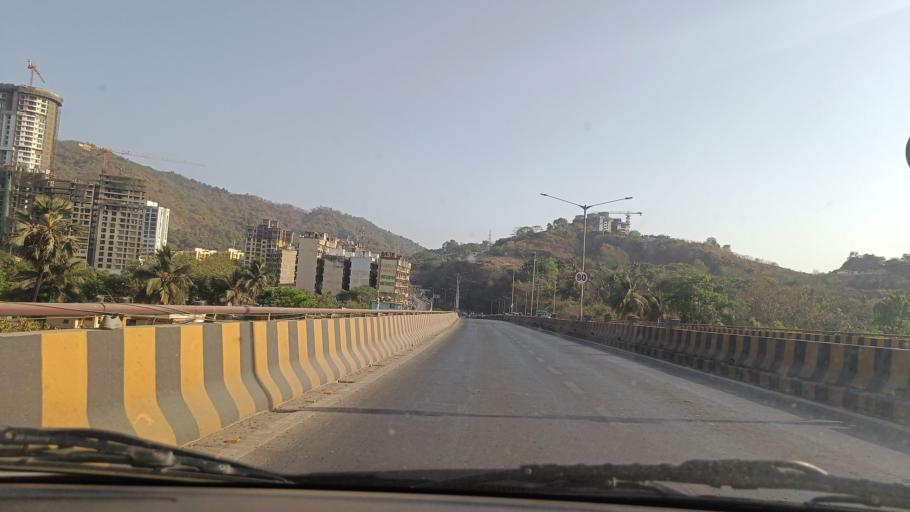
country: IN
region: Maharashtra
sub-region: Mumbai Suburban
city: Mumbai
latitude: 19.0436
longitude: 72.9089
